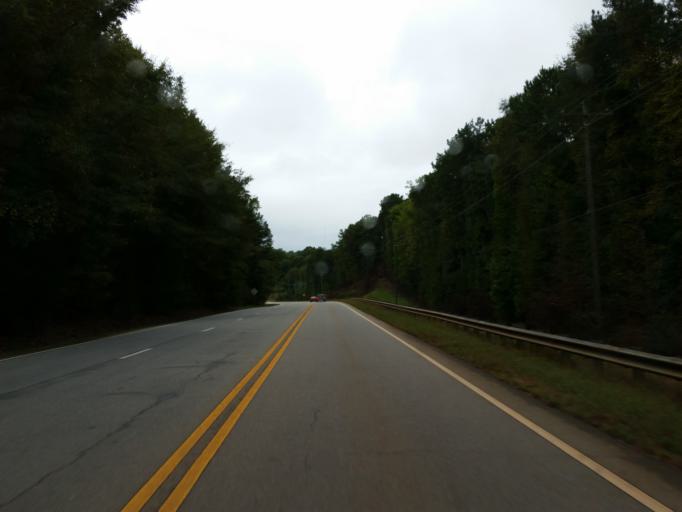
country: US
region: Georgia
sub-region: Lamar County
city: Barnesville
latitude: 32.9043
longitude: -84.0774
